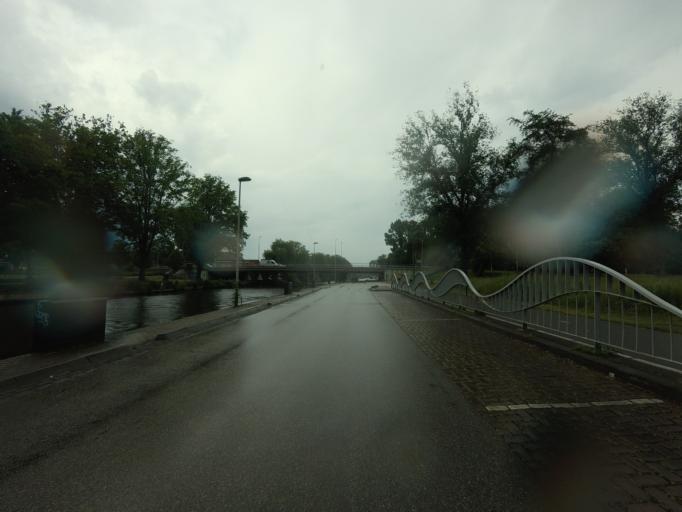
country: NL
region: Utrecht
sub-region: Gemeente Utrecht
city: Utrecht
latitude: 52.1106
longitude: 5.1029
